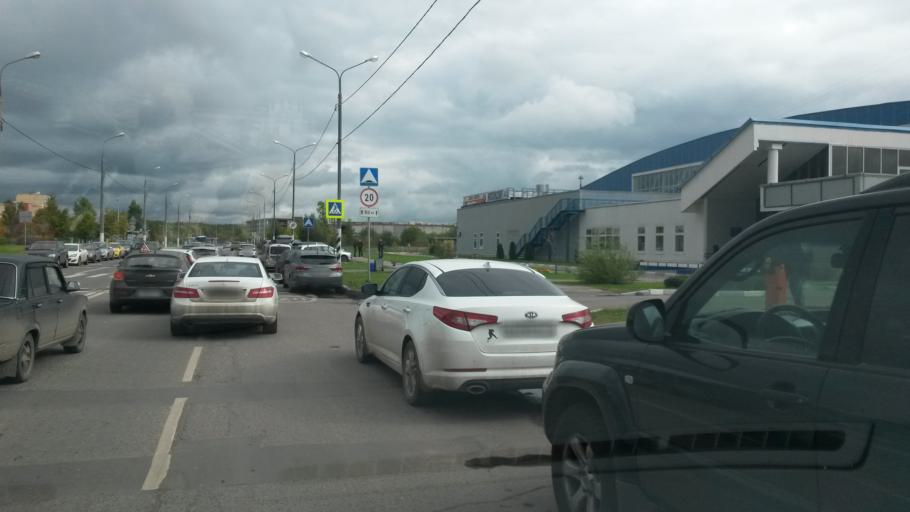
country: RU
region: Moskovskaya
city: Shcherbinka
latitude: 55.5309
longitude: 37.5284
